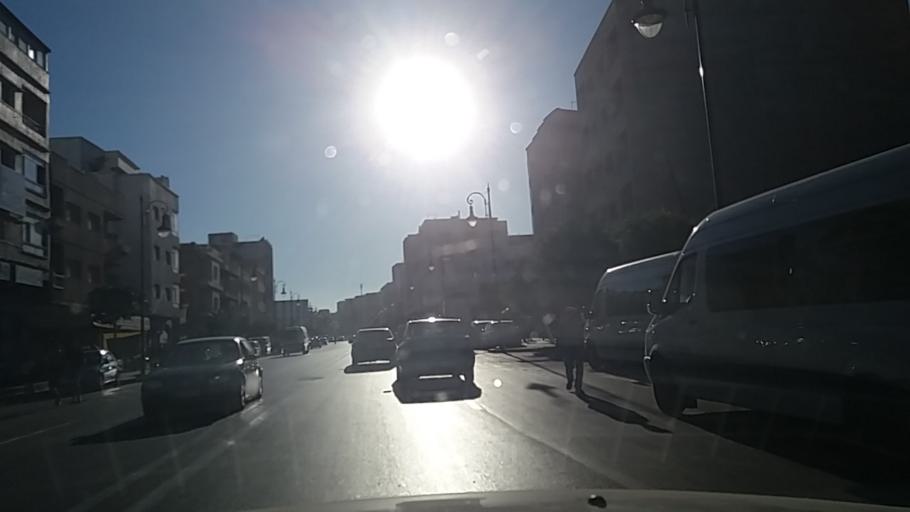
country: MA
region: Tanger-Tetouan
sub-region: Tanger-Assilah
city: Tangier
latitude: 35.7541
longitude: -5.8134
